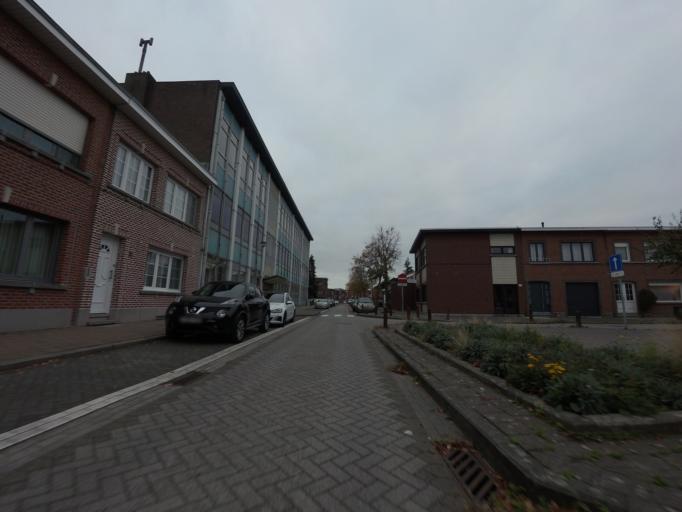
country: BE
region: Flanders
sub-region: Provincie Antwerpen
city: Antwerpen
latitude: 51.2544
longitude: 4.4400
